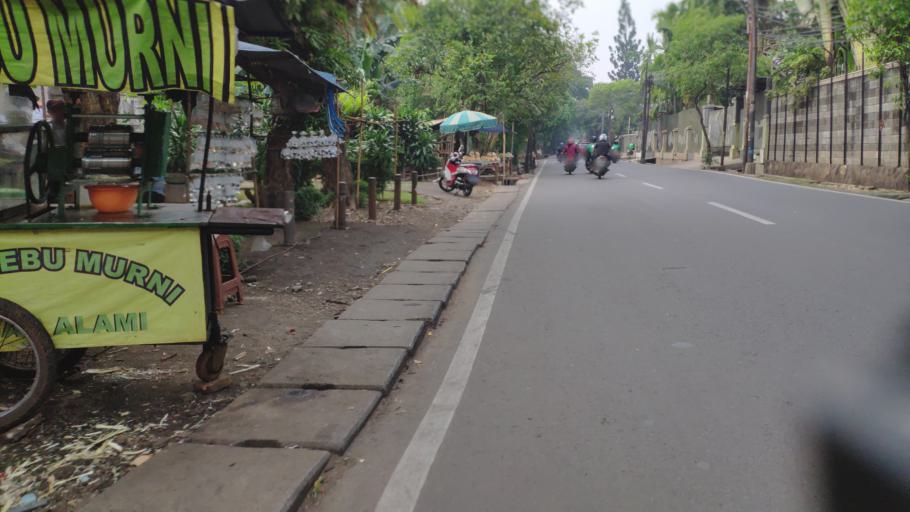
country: ID
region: West Java
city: Pamulang
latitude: -6.3108
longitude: 106.8162
